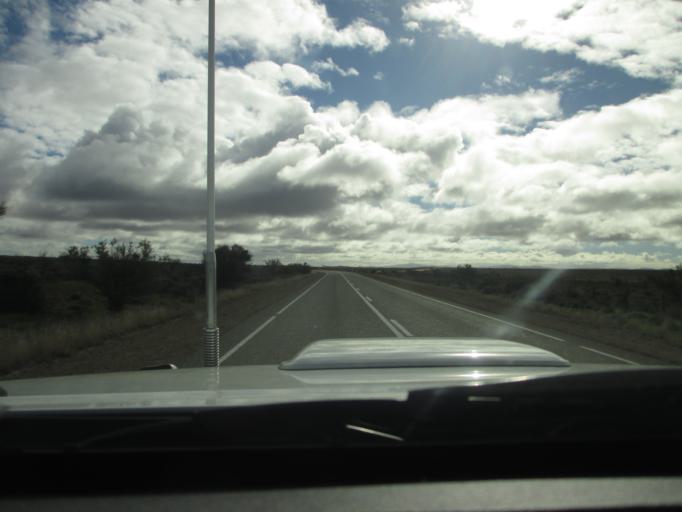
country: AU
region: South Australia
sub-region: Flinders Ranges
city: Quorn
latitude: -32.1803
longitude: 138.5386
